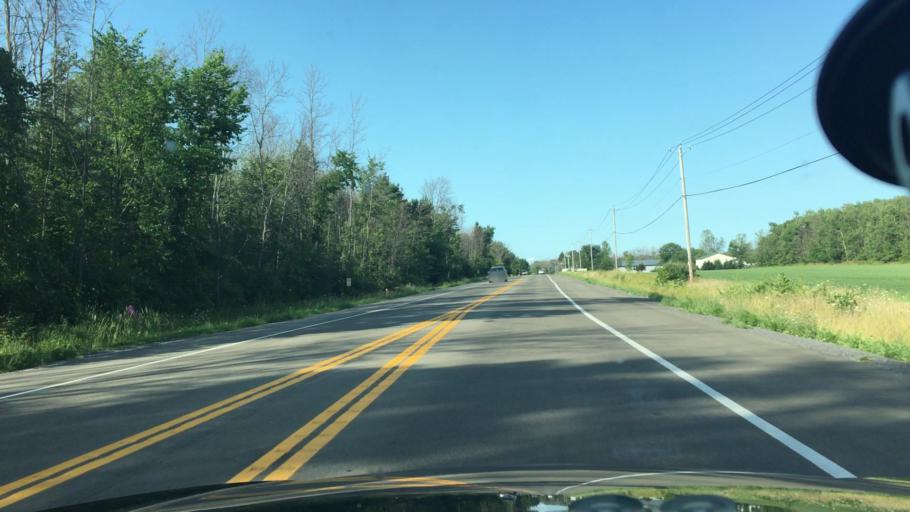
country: US
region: New York
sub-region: Erie County
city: Eden
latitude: 42.6758
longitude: -78.9540
